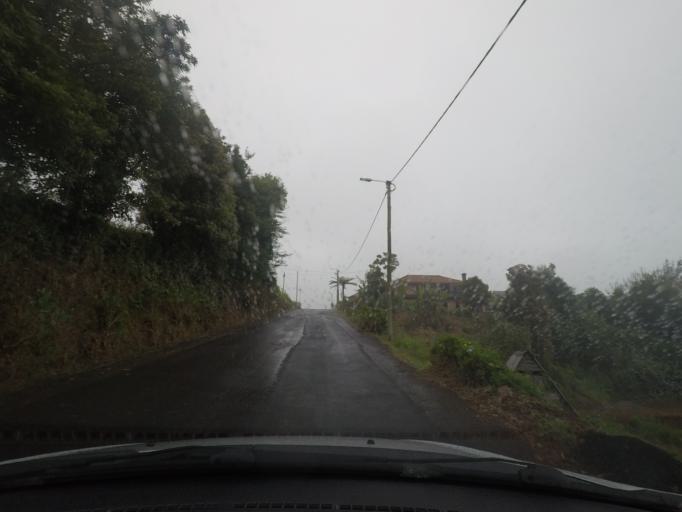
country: PT
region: Madeira
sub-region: Santana
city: Santana
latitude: 32.7942
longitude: -16.8676
